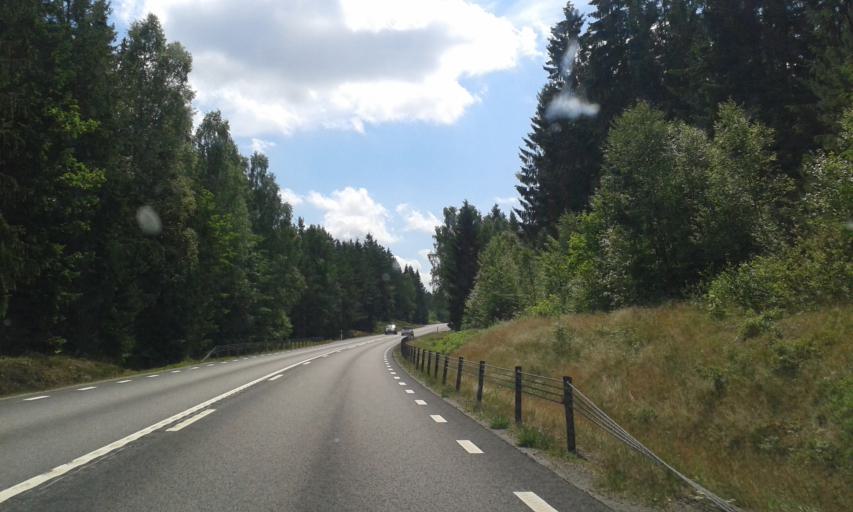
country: SE
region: Joenkoeping
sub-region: Varnamo Kommun
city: Rydaholm
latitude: 56.9222
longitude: 14.4191
